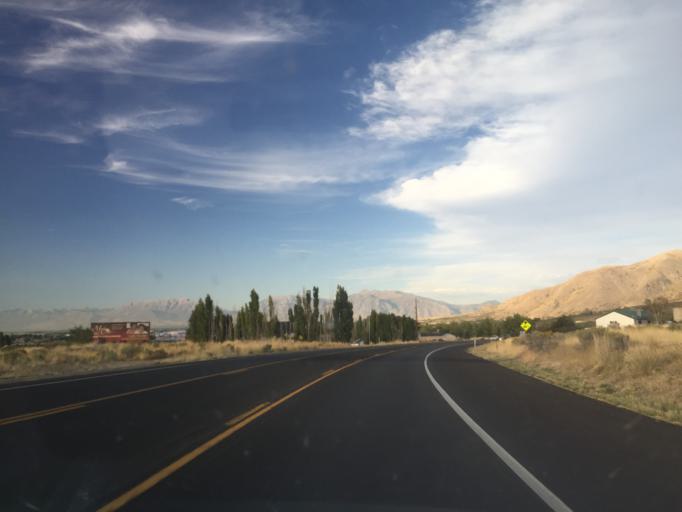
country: US
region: Utah
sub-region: Utah County
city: Santaquin
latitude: 39.9834
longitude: -111.7655
